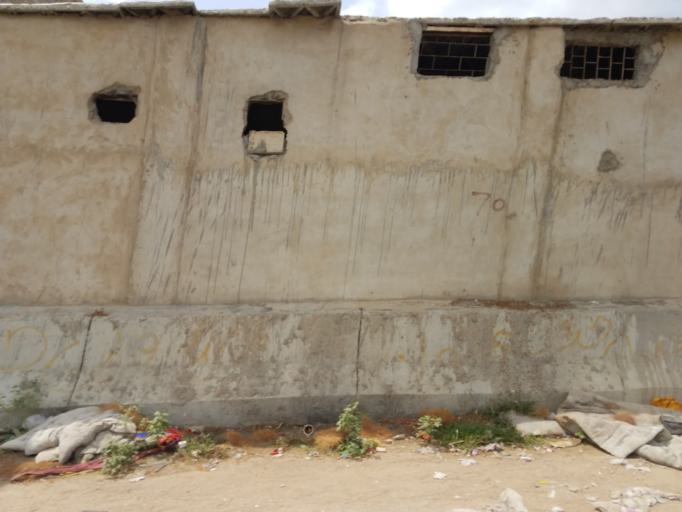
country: PK
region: Sindh
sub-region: Karachi District
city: Karachi
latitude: 24.9412
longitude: 67.0888
